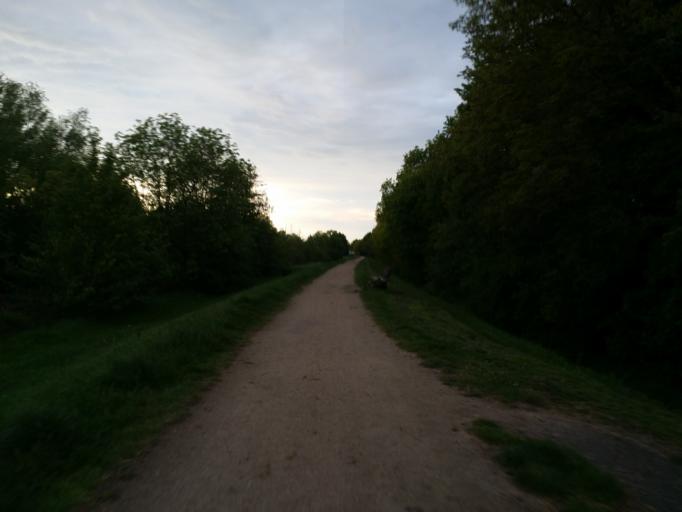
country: DE
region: Lower Saxony
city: Stuhr
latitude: 53.0568
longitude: 8.7699
